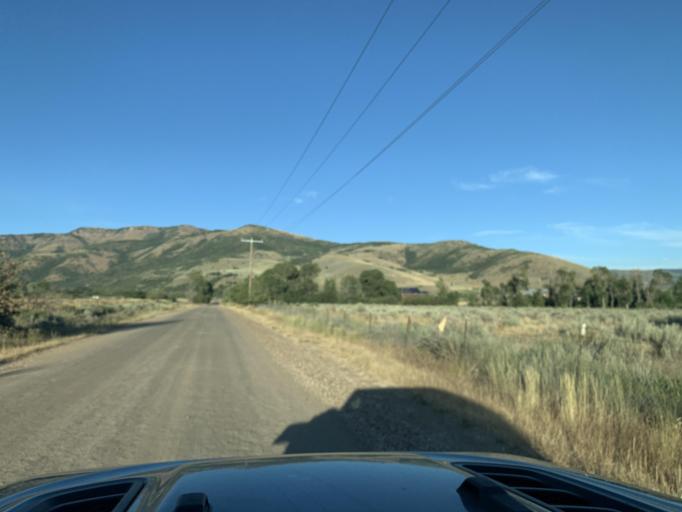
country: US
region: Utah
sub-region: Weber County
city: Wolf Creek
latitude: 41.2932
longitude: -111.7645
